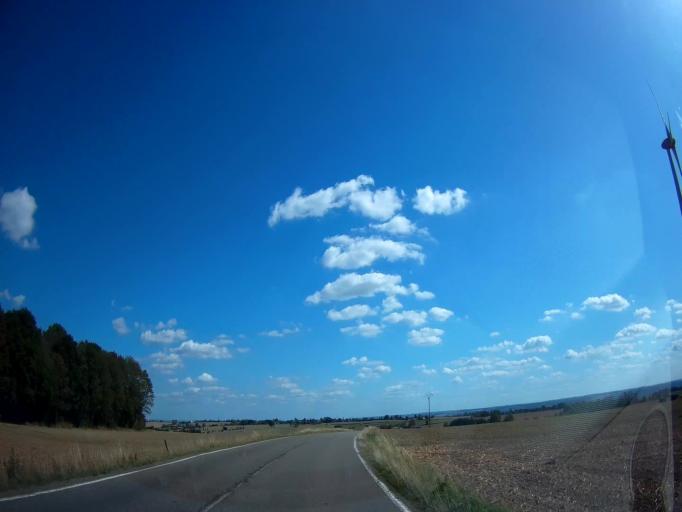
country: FR
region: Champagne-Ardenne
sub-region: Departement des Ardennes
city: Fromelennes
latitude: 50.1782
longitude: 4.8648
